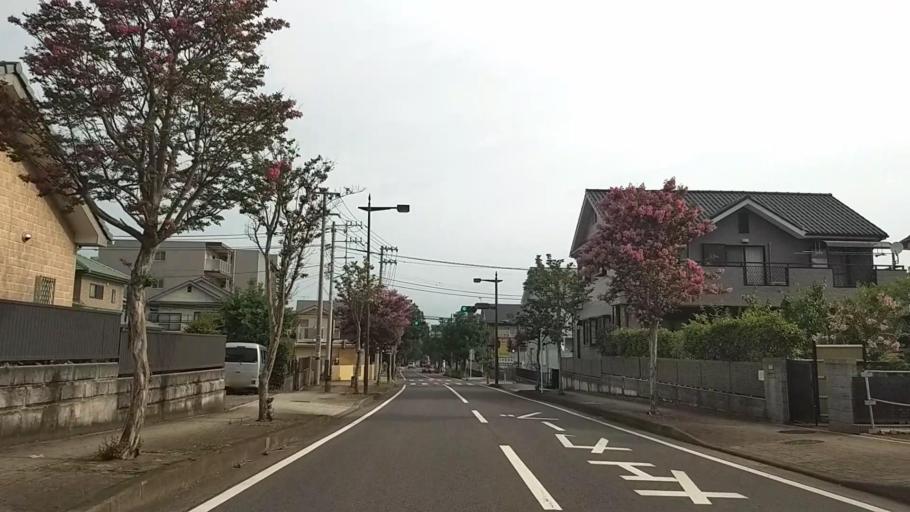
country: JP
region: Kanagawa
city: Oiso
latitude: 35.3296
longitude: 139.3097
